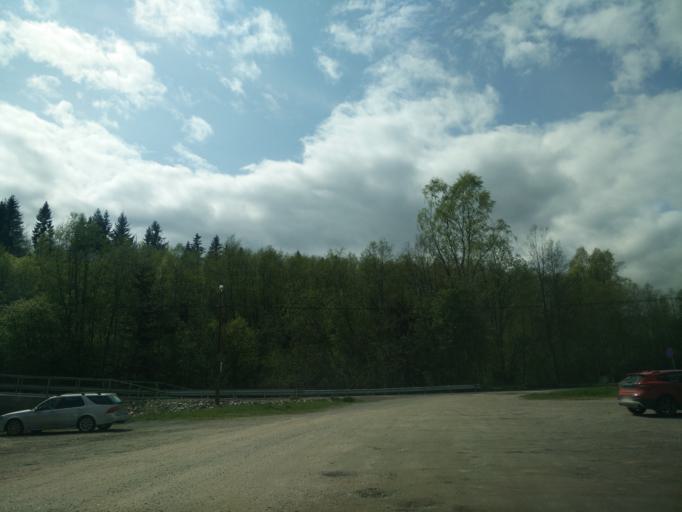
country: SE
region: Vaesternorrland
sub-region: Sundsvalls Kommun
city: Sundsvall
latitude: 62.3671
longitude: 17.2710
